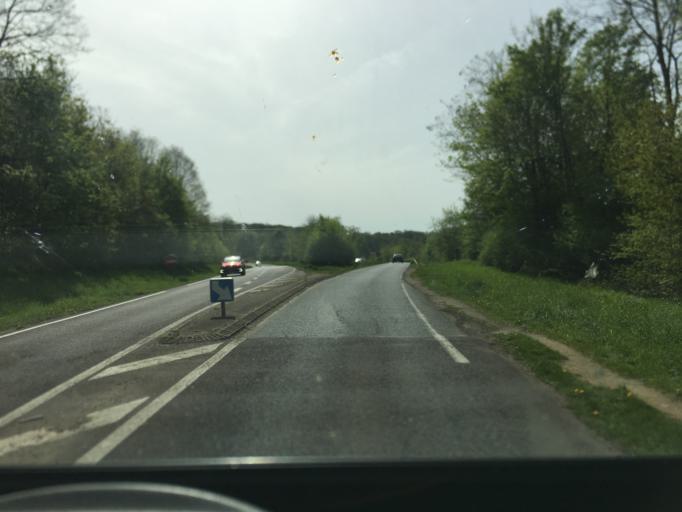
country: FR
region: Lorraine
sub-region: Departement de Meurthe-et-Moselle
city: Messein
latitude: 48.6057
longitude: 6.1523
